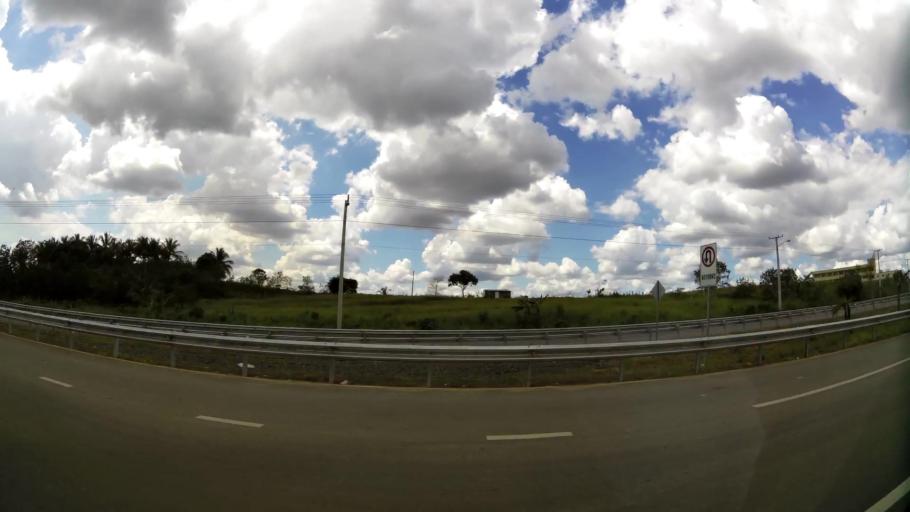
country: DO
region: Nacional
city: Santo Domingo
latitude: 18.5612
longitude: -69.9773
